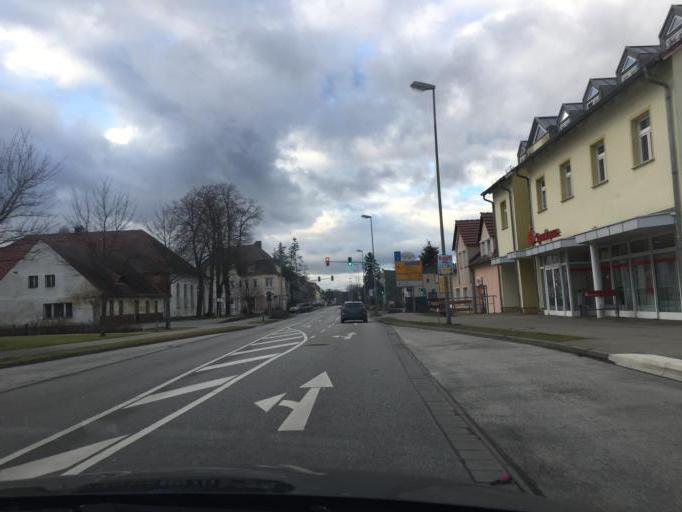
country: DE
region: Brandenburg
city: Kolkwitz
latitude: 51.7498
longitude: 14.2461
